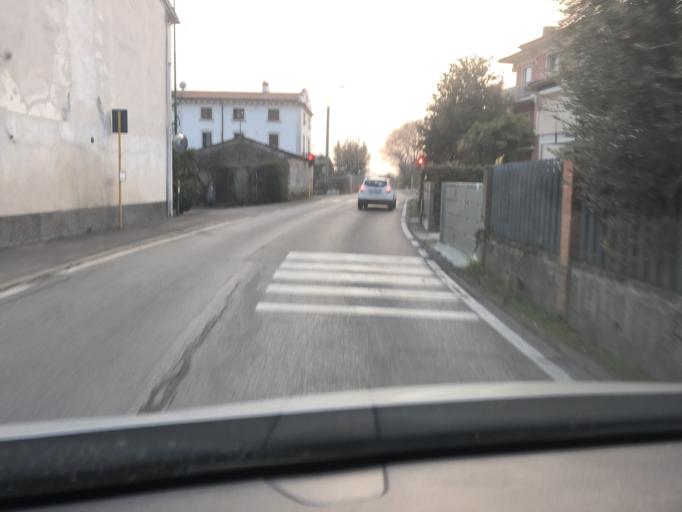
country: IT
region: Veneto
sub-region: Provincia di Verona
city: Sommacampagna
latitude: 45.4015
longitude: 10.8418
